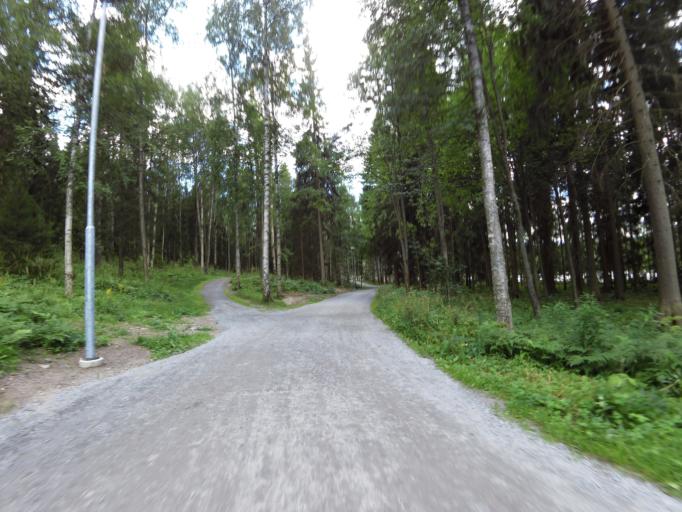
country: FI
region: Pirkanmaa
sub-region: Tampere
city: Yloejaervi
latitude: 61.5097
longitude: 23.6164
